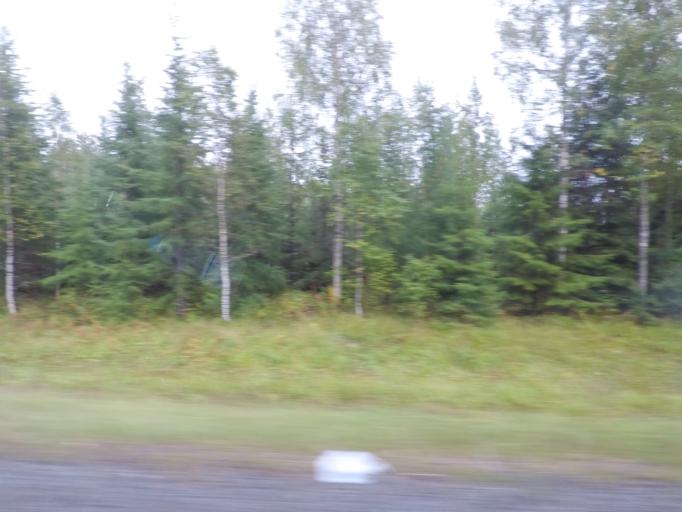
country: FI
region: Southern Savonia
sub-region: Pieksaemaeki
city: Juva
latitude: 62.0074
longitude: 27.8017
